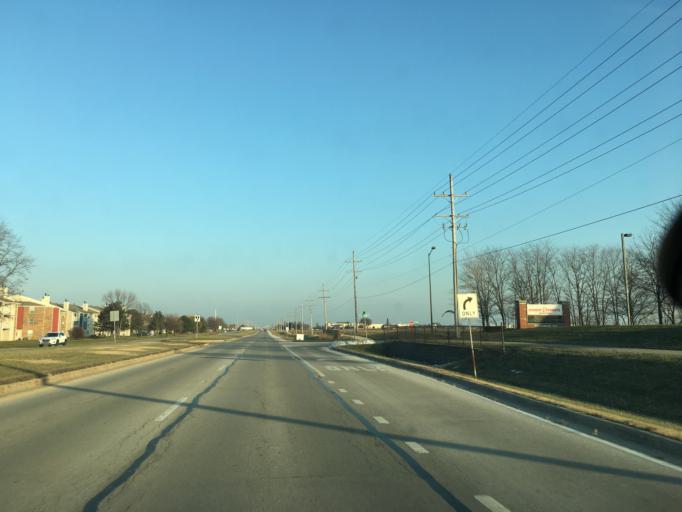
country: US
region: Illinois
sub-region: DuPage County
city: Naperville
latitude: 41.7469
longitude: -88.2170
